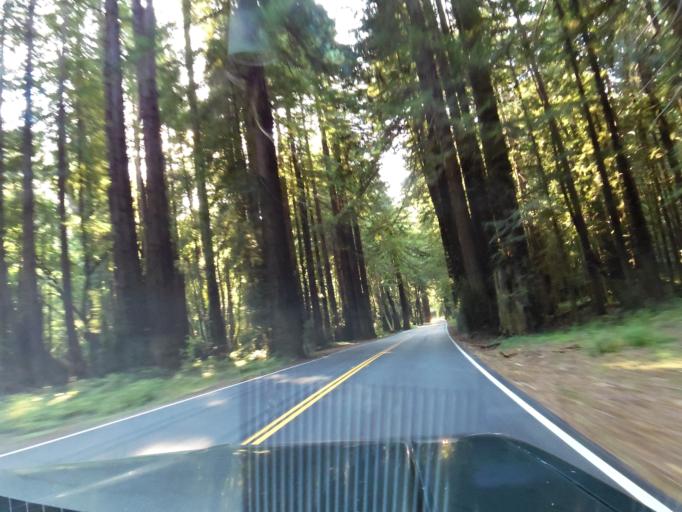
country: US
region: California
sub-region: Mendocino County
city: Boonville
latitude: 39.1561
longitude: -123.6282
